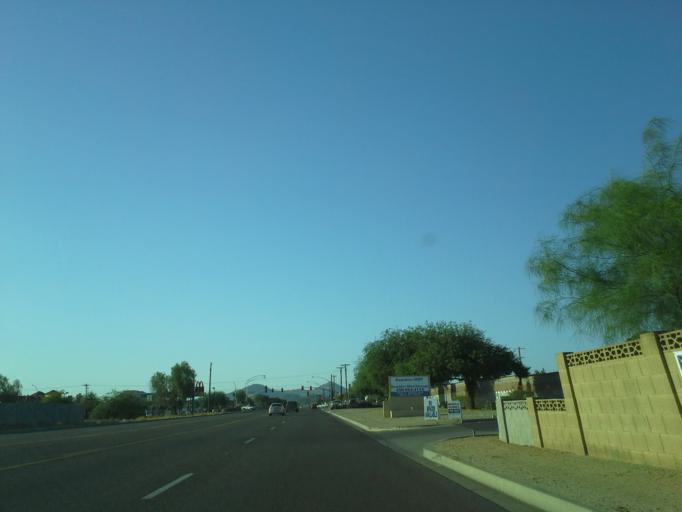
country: US
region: Arizona
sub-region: Pinal County
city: Apache Junction
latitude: 33.4129
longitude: -111.6326
